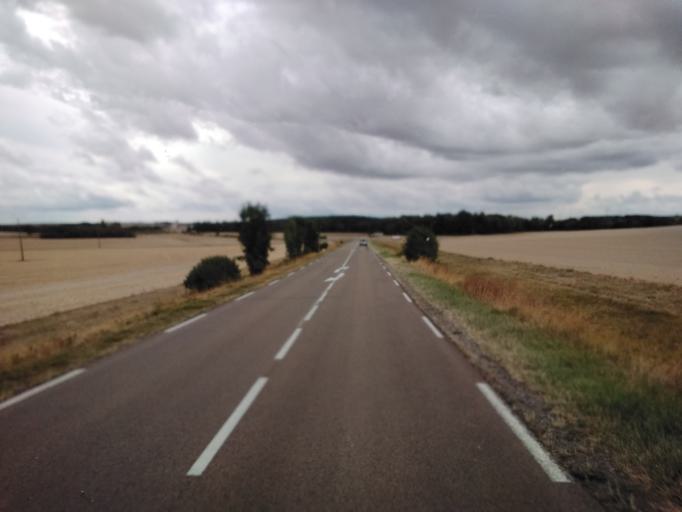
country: FR
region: Champagne-Ardenne
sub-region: Departement de la Marne
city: Frignicourt
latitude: 48.5950
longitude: 4.5456
